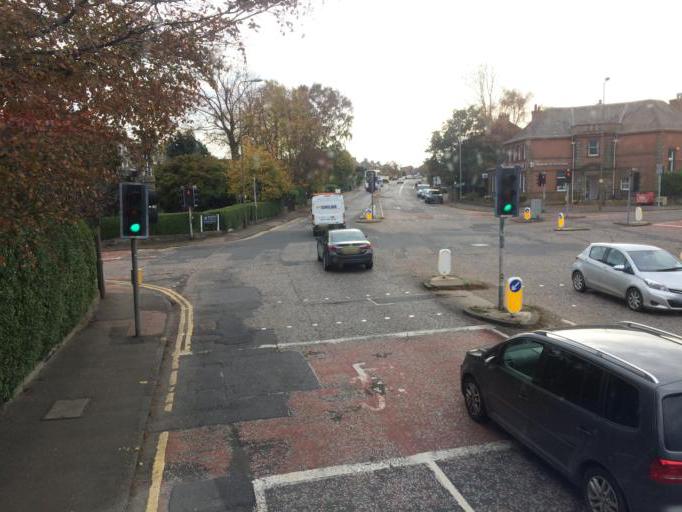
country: GB
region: Scotland
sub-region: Midlothian
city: Loanhead
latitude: 55.9129
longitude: -3.1634
